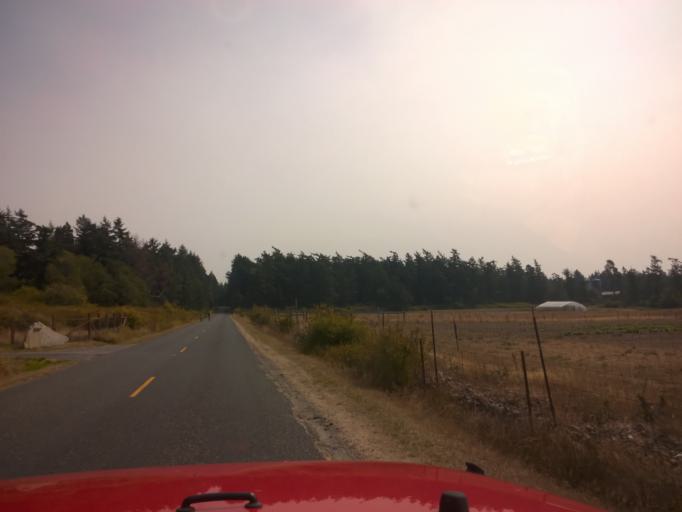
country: US
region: Washington
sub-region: San Juan County
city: Friday Harbor
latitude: 48.5322
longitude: -122.8721
